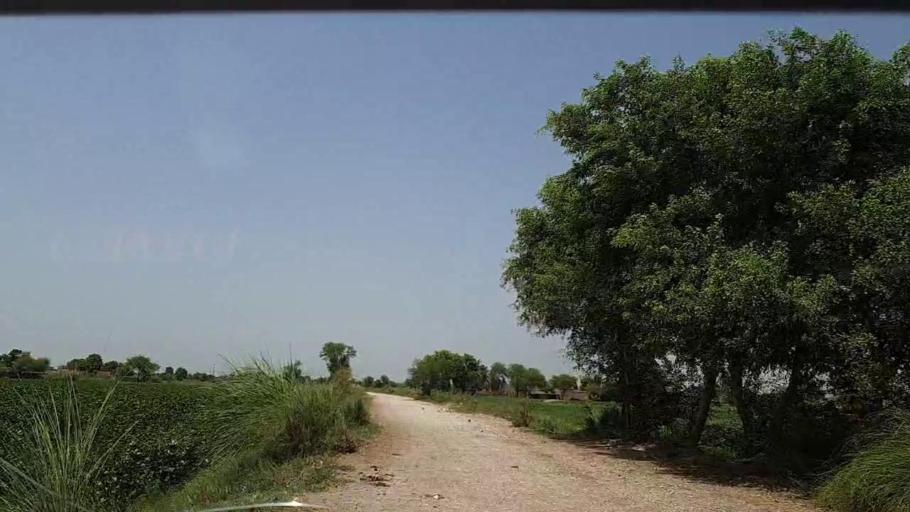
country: PK
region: Sindh
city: Tharu Shah
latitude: 26.9468
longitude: 68.0445
